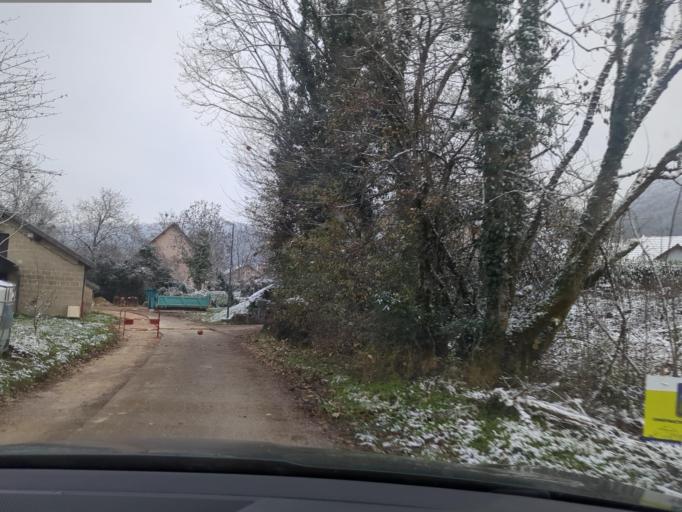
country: FR
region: Franche-Comte
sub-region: Departement du Jura
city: Perrigny
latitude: 46.6604
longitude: 5.5872
